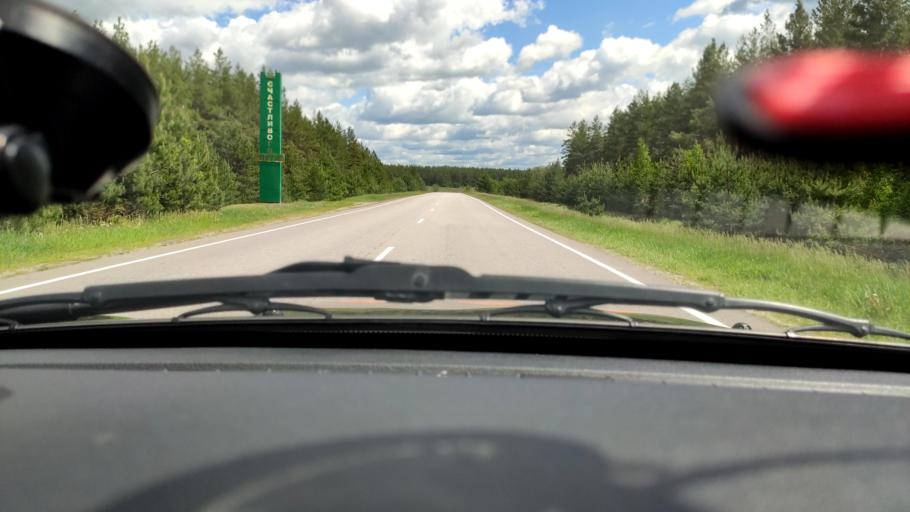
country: RU
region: Voronezj
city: Uryv-Pokrovka
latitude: 51.0537
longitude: 38.9454
